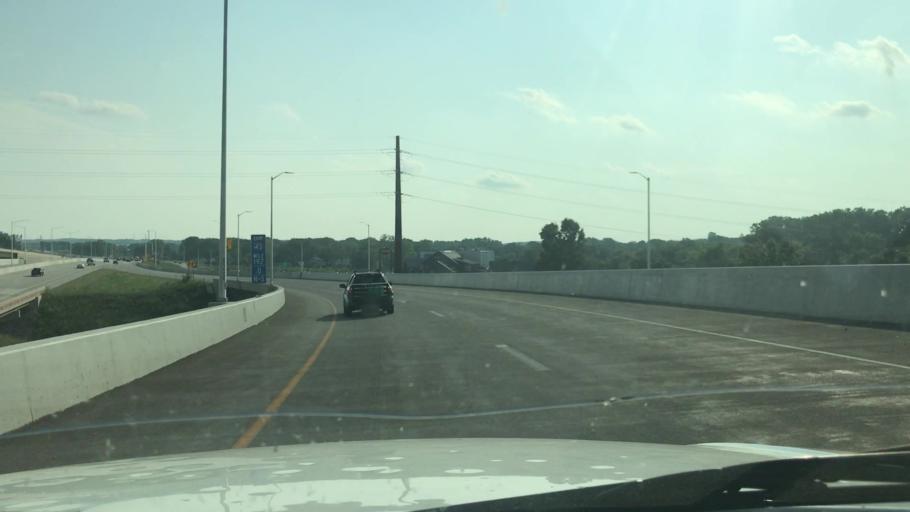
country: US
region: Wisconsin
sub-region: Brown County
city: Howard
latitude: 44.5598
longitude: -88.0542
